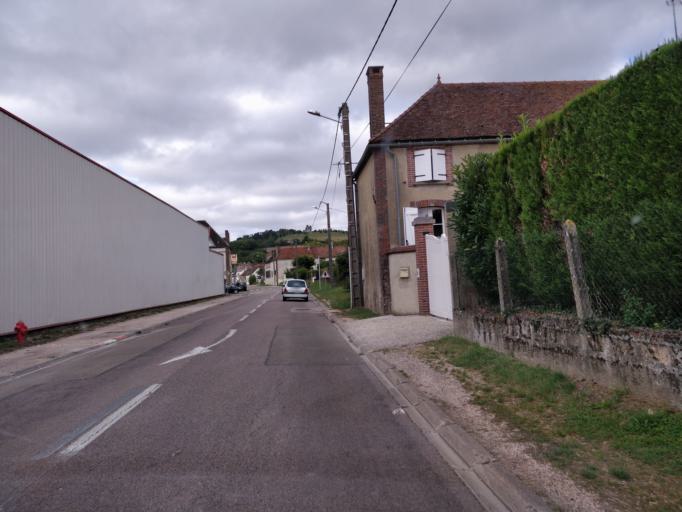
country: FR
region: Bourgogne
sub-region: Departement de l'Yonne
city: Saint-Florentin
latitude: 48.0792
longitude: 3.7031
